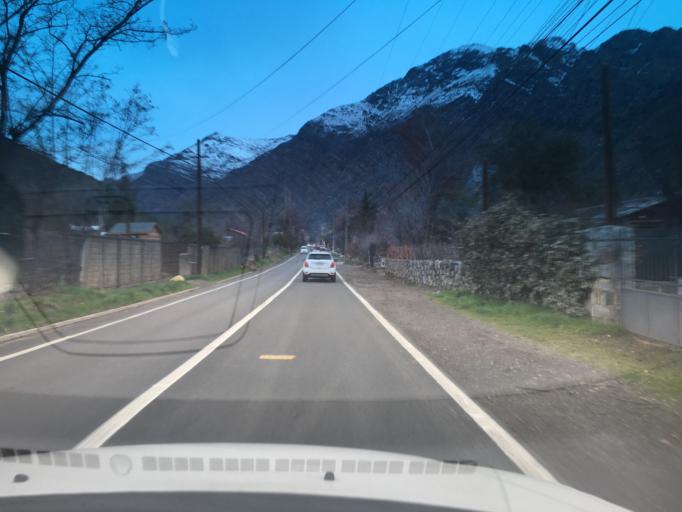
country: CL
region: Santiago Metropolitan
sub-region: Provincia de Cordillera
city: Puente Alto
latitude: -33.7105
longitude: -70.3326
